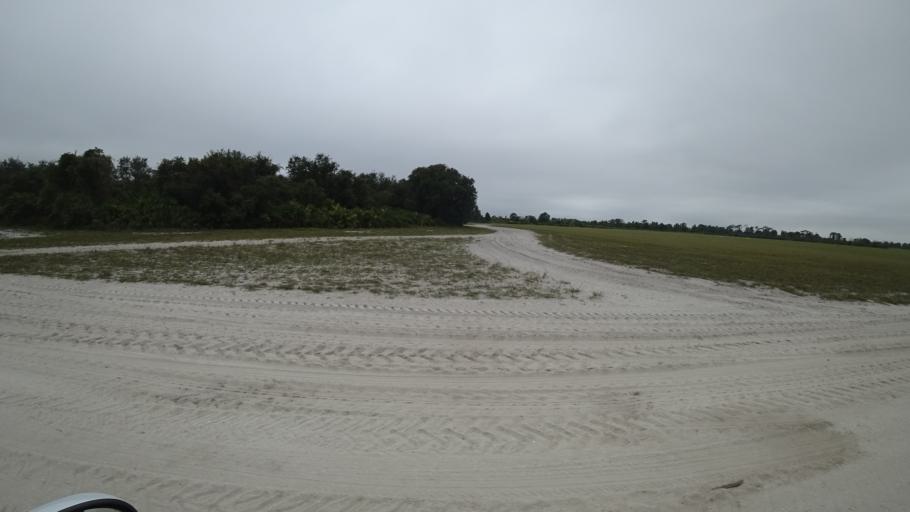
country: US
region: Florida
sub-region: Sarasota County
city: Warm Mineral Springs
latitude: 27.2999
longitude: -82.1266
